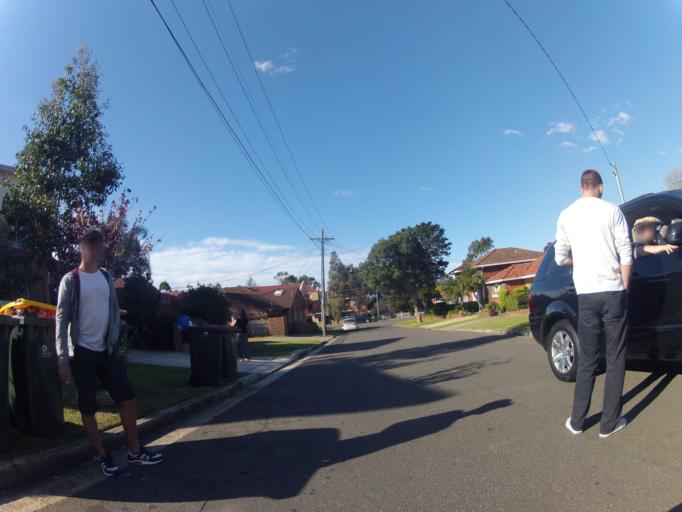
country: AU
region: New South Wales
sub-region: Hurstville
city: Penshurst
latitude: -33.9533
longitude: 151.0801
